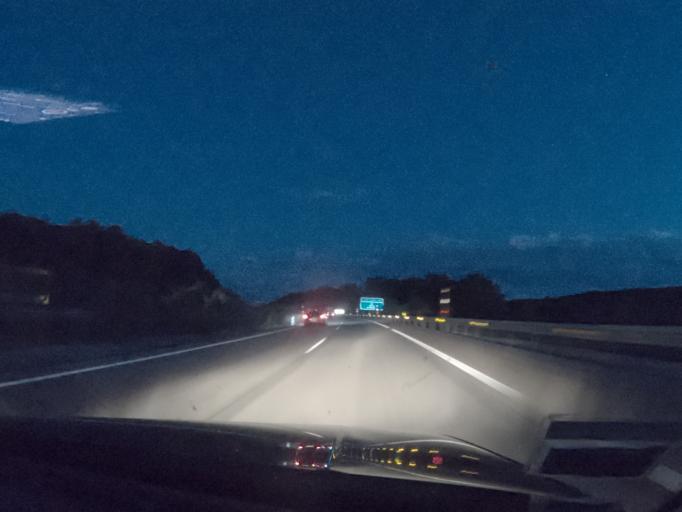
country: ES
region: Castille and Leon
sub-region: Provincia de Leon
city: Villagaton
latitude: 42.5682
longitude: -6.2155
